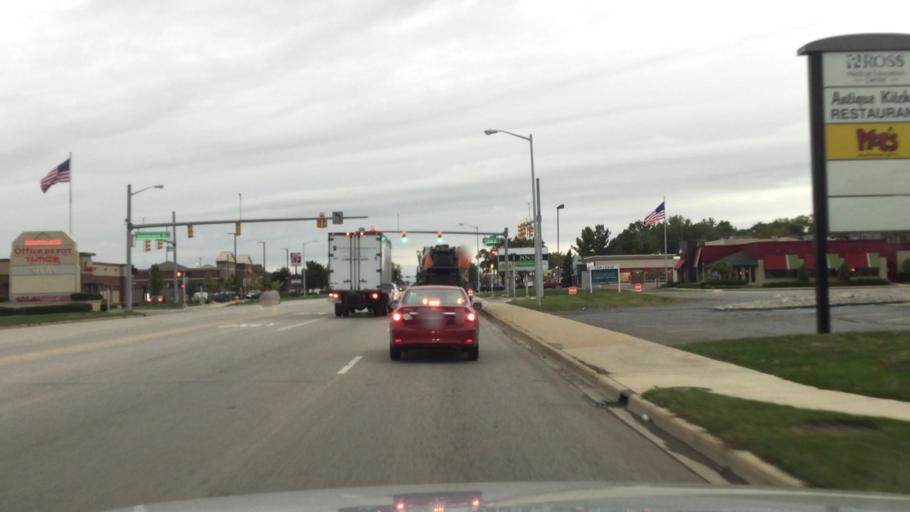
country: US
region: Michigan
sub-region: Kalamazoo County
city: Portage
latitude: 42.2264
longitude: -85.5894
